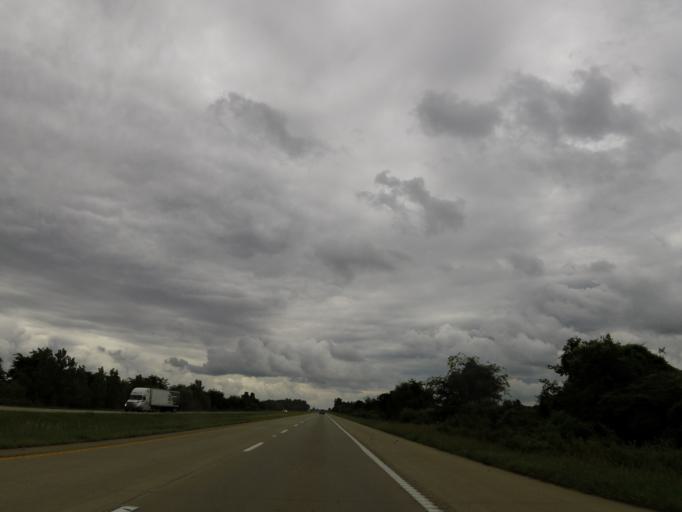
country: US
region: Missouri
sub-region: Mississippi County
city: Charleston
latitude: 36.9438
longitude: -89.2921
